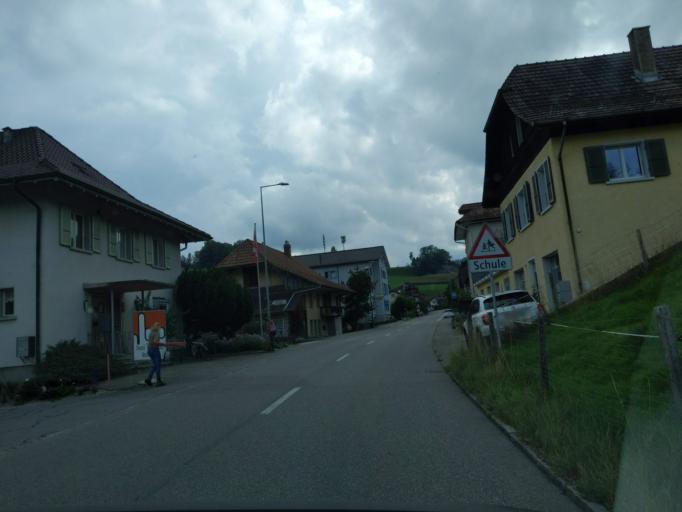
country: CH
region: Bern
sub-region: Oberaargau
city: Wyssachen
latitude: 47.0793
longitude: 7.8281
